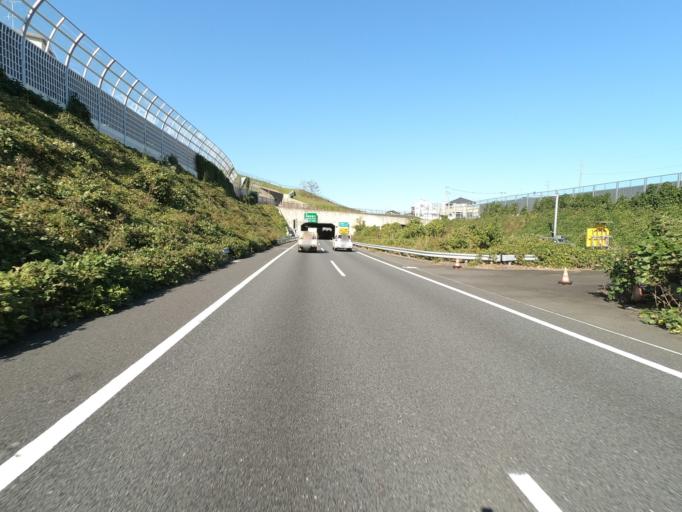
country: JP
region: Kanagawa
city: Zama
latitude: 35.5149
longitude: 139.3604
